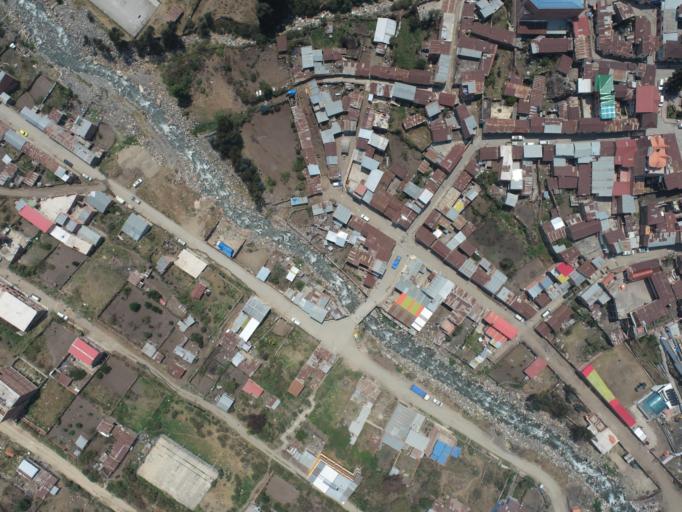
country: BO
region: La Paz
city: Quime
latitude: -16.9786
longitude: -67.2159
